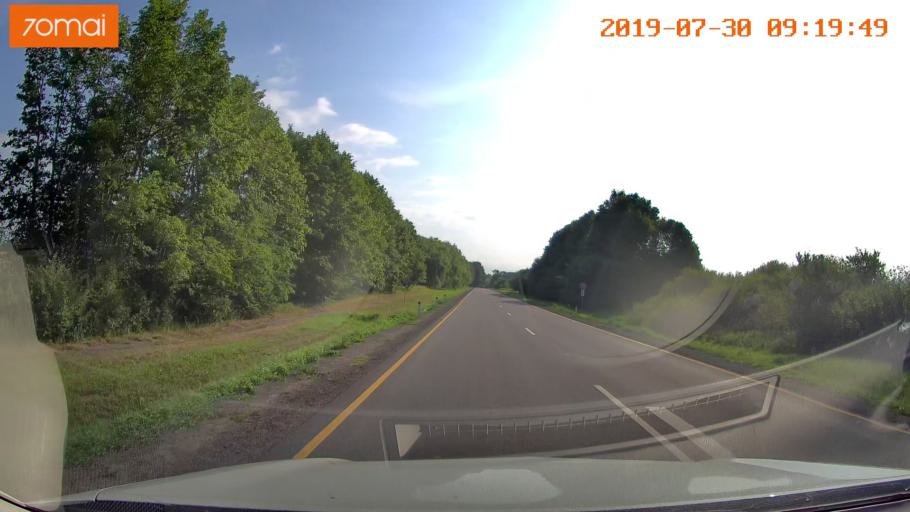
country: RU
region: Kaliningrad
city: Nesterov
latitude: 54.6337
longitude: 22.5983
